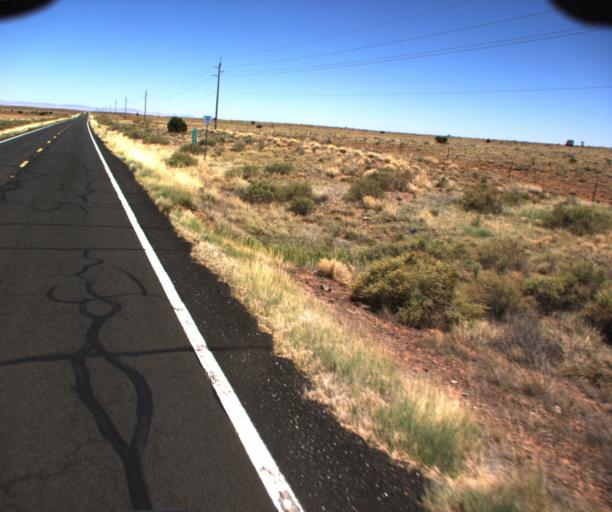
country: US
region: Arizona
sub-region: Coconino County
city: LeChee
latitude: 34.8694
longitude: -110.9032
